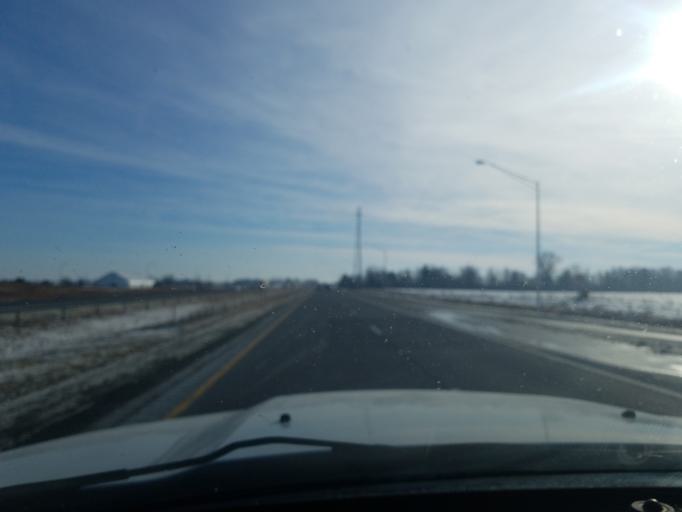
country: US
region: Indiana
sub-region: Grant County
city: Fairmount
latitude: 40.3538
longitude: -85.5589
